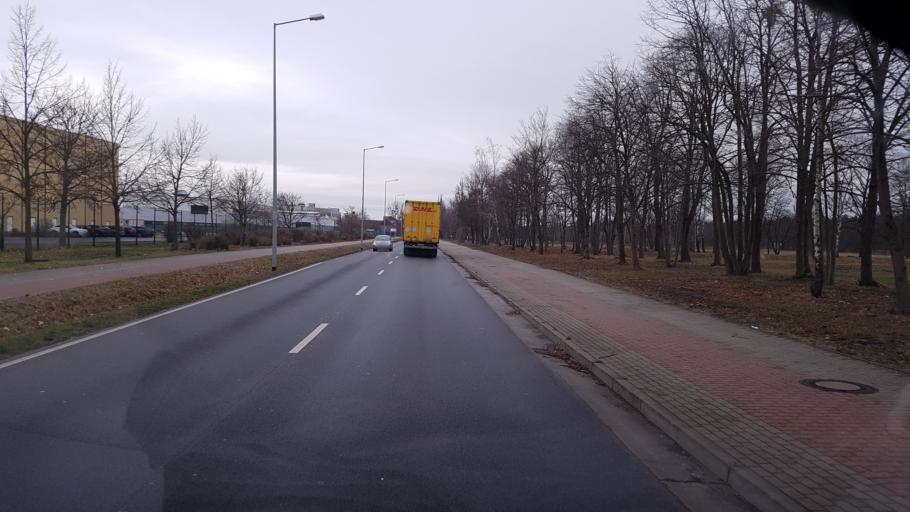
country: DE
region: Brandenburg
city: Schwarzheide
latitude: 51.4847
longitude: 13.8838
